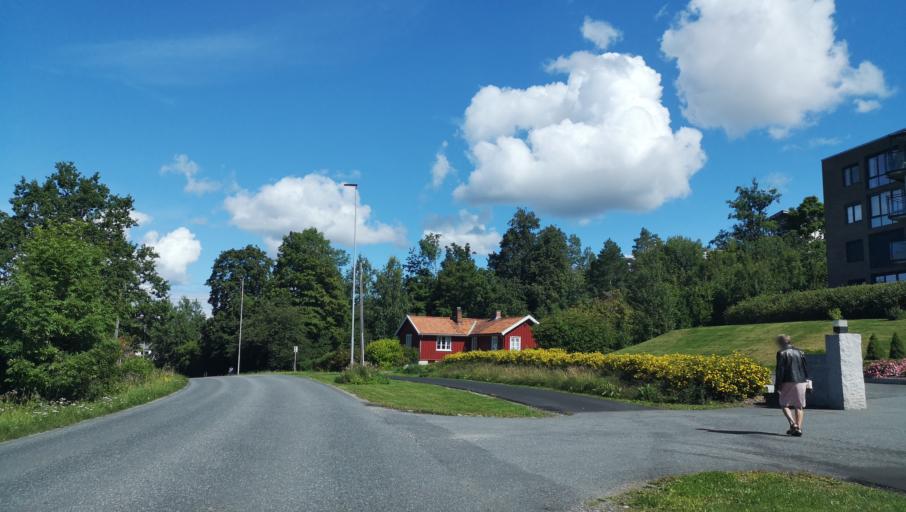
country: NO
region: Akershus
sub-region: Frogn
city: Drobak
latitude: 59.6614
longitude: 10.6402
